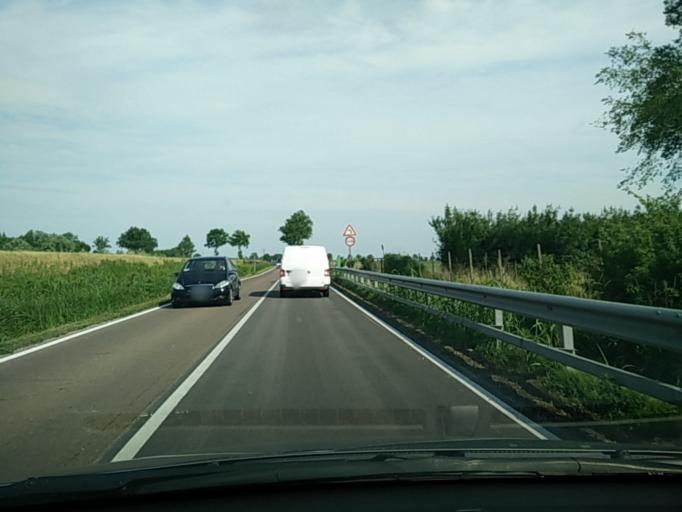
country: IT
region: Veneto
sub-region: Provincia di Venezia
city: Quarto d'Altino
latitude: 45.5619
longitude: 12.4219
